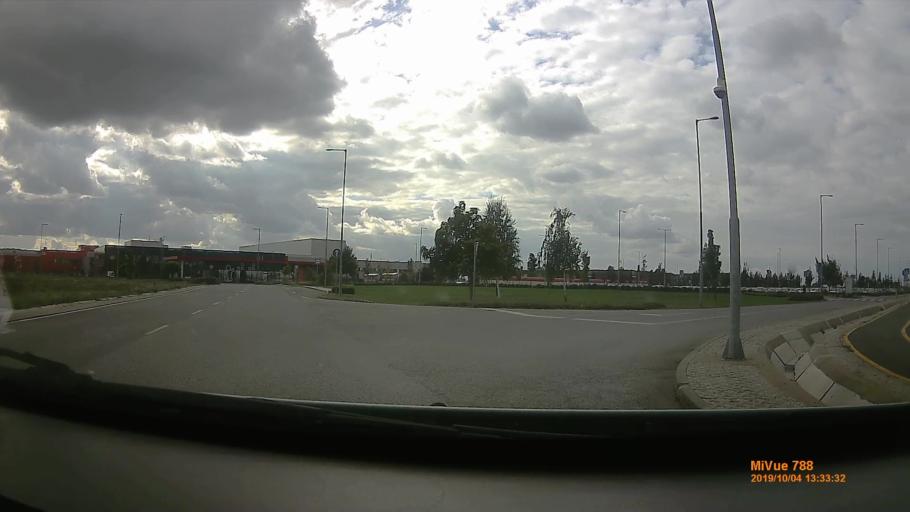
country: HU
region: Szabolcs-Szatmar-Bereg
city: Nyirtelek
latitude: 47.9529
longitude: 21.6491
